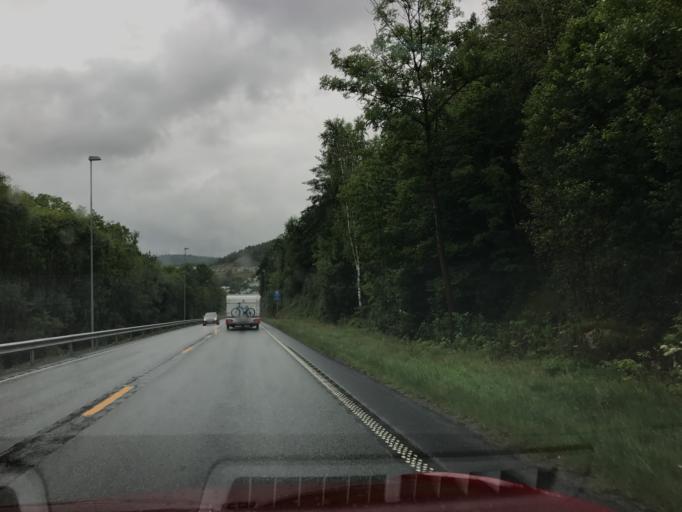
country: NO
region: Vest-Agder
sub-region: Lyngdal
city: Lyngdal
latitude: 58.1570
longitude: 7.1232
